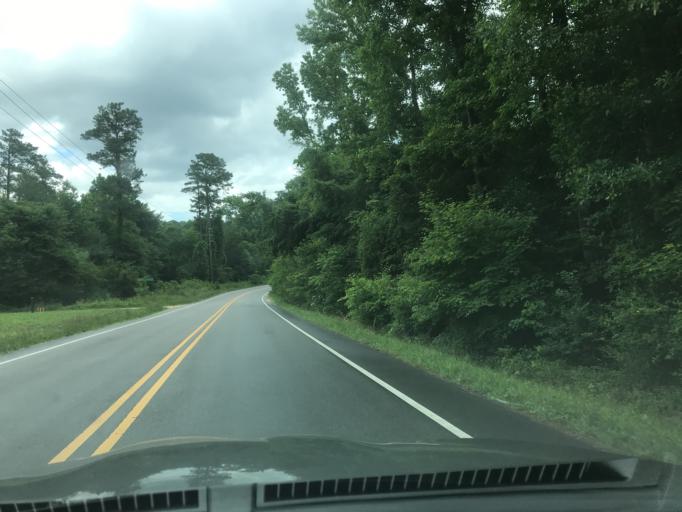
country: US
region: North Carolina
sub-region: Wake County
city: Knightdale
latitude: 35.8367
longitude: -78.4832
